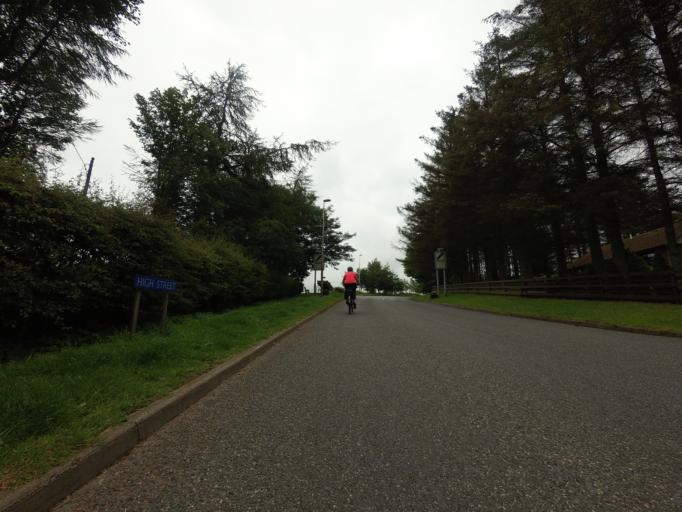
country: GB
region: Scotland
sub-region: Aberdeenshire
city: Turriff
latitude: 57.5441
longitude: -2.3208
